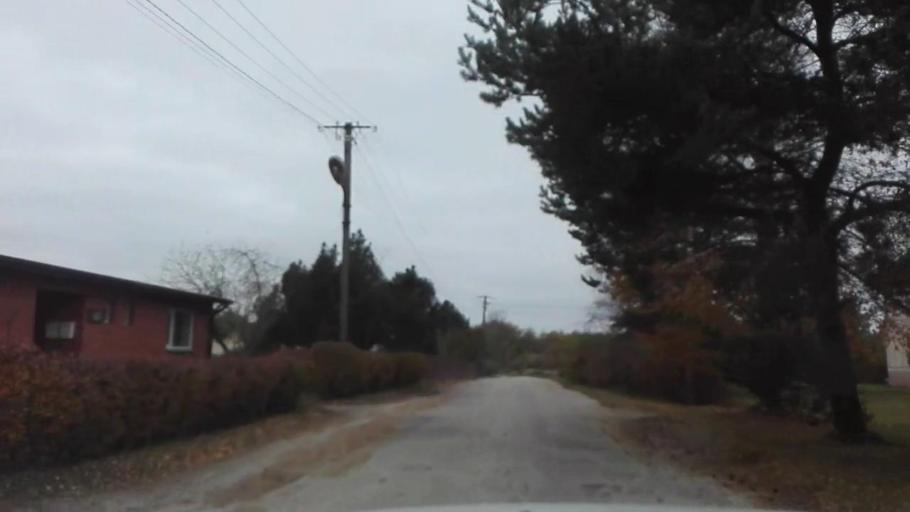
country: EE
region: Jogevamaa
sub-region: Poltsamaa linn
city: Poltsamaa
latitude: 58.4259
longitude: 26.0301
